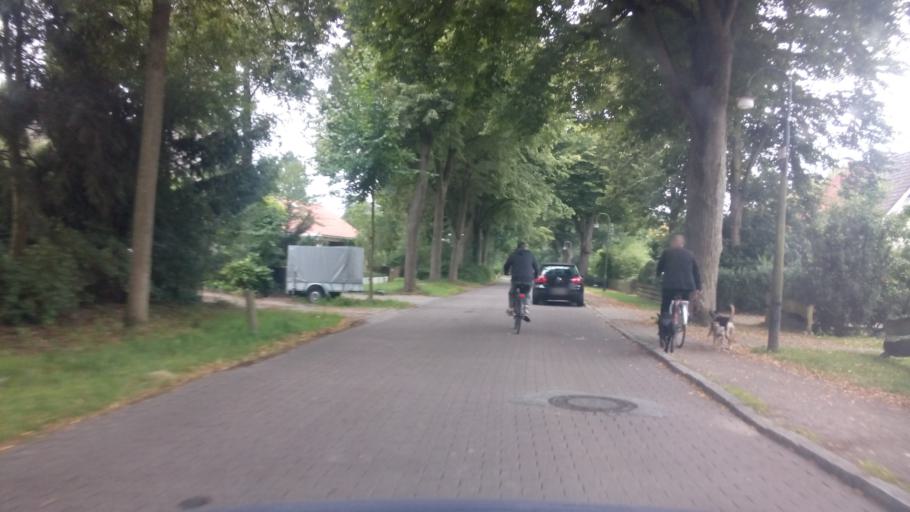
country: DE
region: Lower Saxony
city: Lilienthal
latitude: 53.1198
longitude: 8.8913
